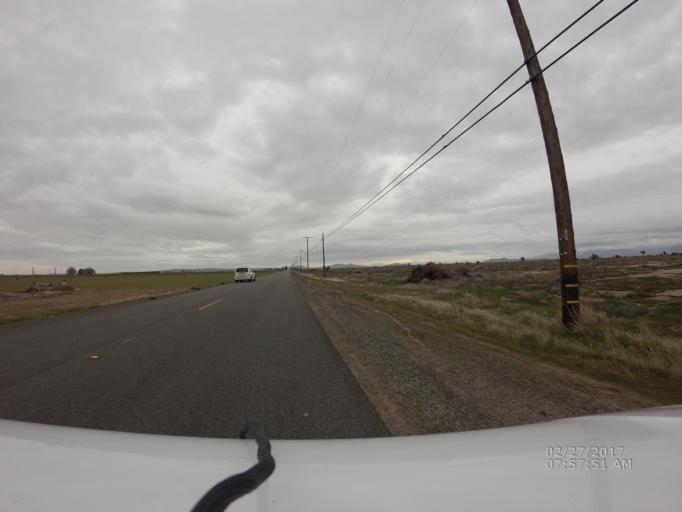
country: US
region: California
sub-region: Los Angeles County
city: Lancaster
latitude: 34.7047
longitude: -118.0014
